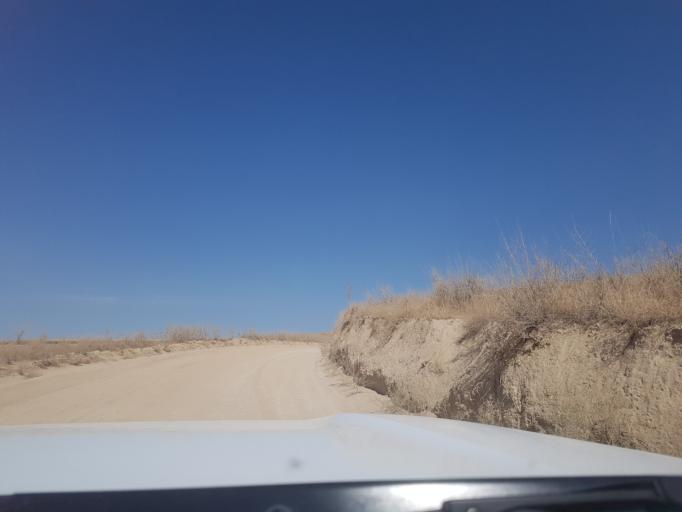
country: TM
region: Ahal
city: Baharly
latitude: 38.2714
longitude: 56.8952
